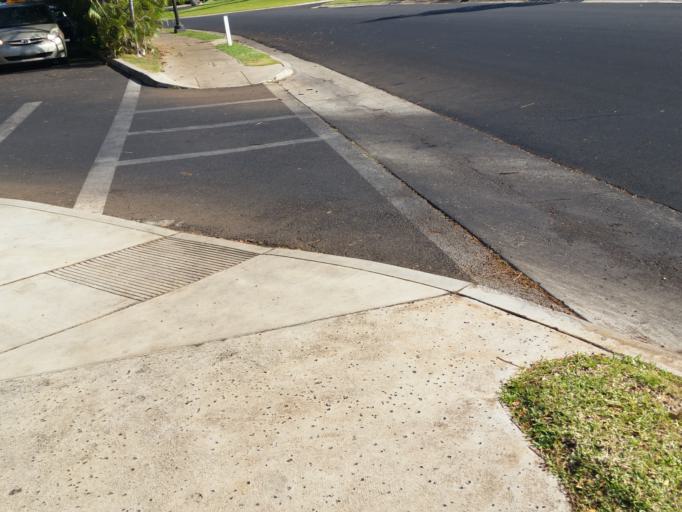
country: US
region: Hawaii
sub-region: Maui County
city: Ka'anapali
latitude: 20.9265
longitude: -156.6933
